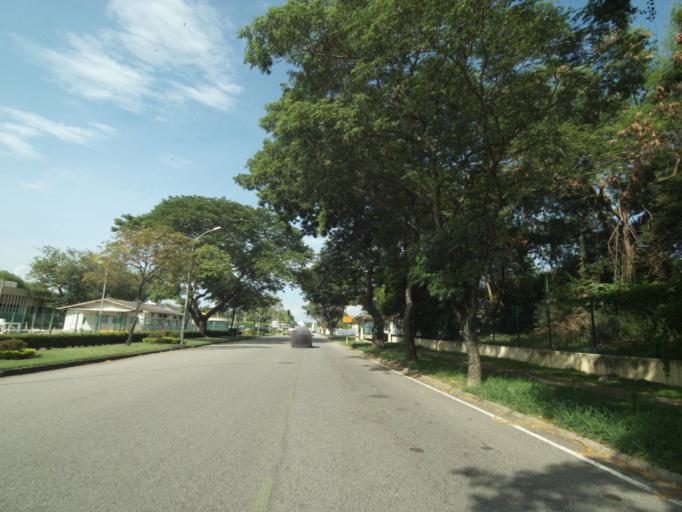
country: BR
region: Rio de Janeiro
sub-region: Rio De Janeiro
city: Rio de Janeiro
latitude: -22.8559
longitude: -43.2333
